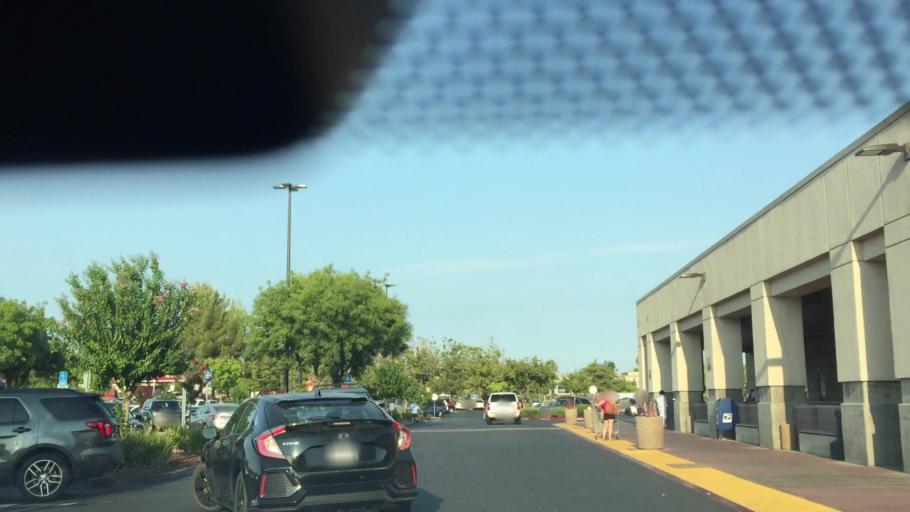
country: US
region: California
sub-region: Placer County
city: Rocklin
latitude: 38.7806
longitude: -121.2679
